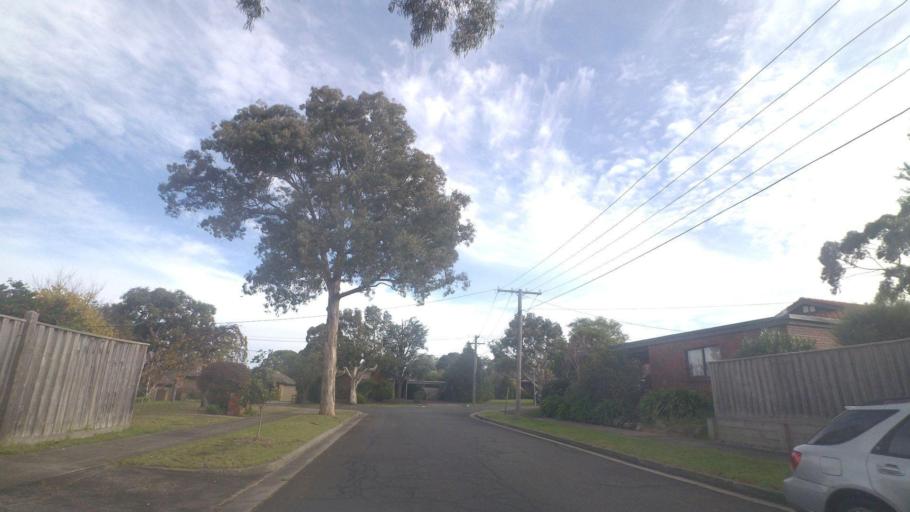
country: AU
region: Victoria
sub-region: Whitehorse
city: Vermont South
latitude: -37.8599
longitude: 145.1900
